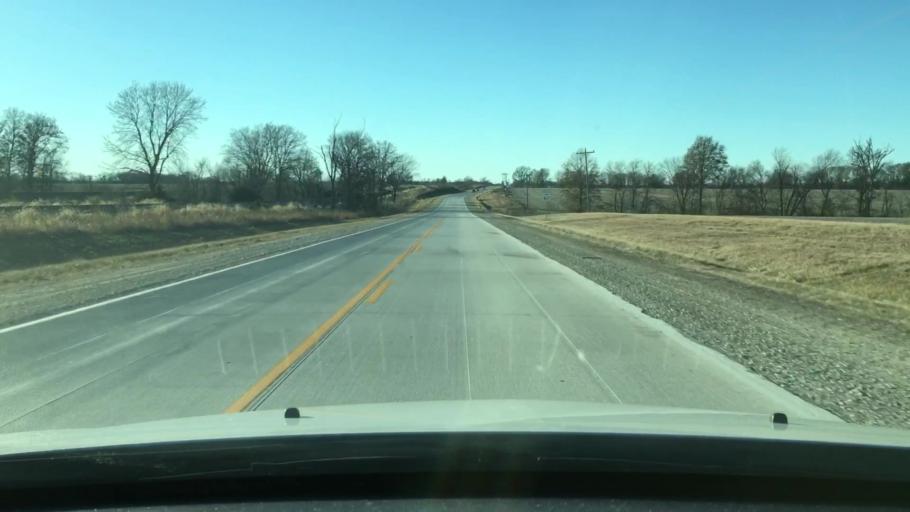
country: US
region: Missouri
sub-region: Boone County
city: Centralia
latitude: 39.2014
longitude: -92.0645
